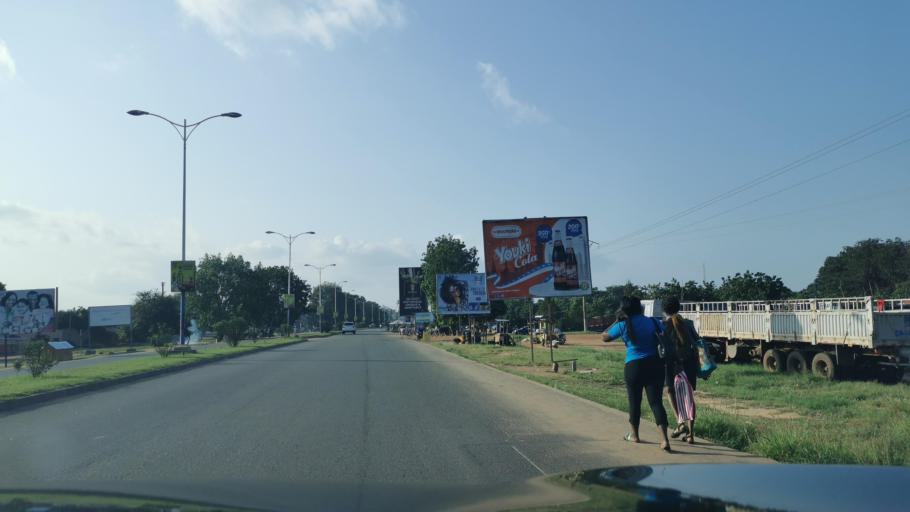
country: TG
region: Maritime
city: Lome
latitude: 6.2001
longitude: 1.2087
